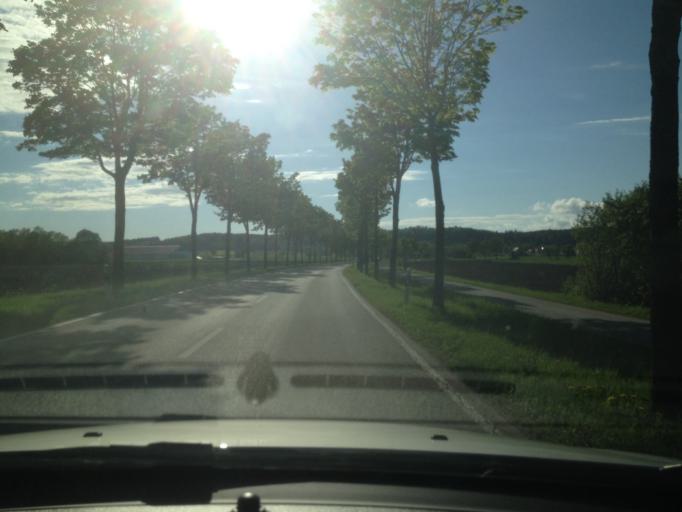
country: DE
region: Bavaria
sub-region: Swabia
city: Bobingen
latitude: 48.3124
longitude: 10.8322
